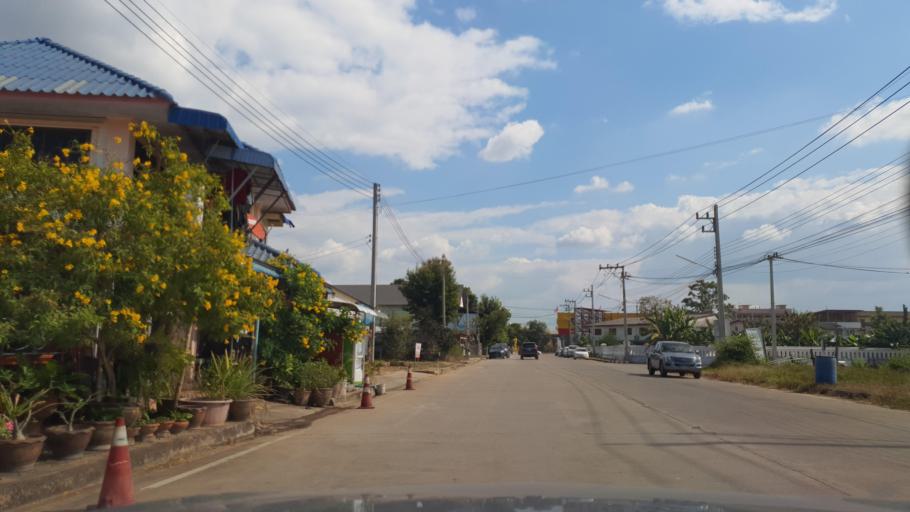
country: TH
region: Nan
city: Nan
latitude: 18.7871
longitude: 100.7738
